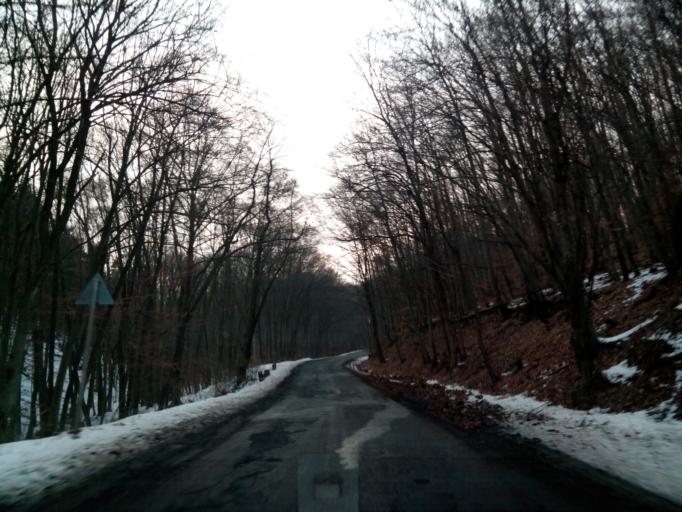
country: HU
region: Borsod-Abauj-Zemplen
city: Gonc
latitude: 48.4884
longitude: 21.4034
